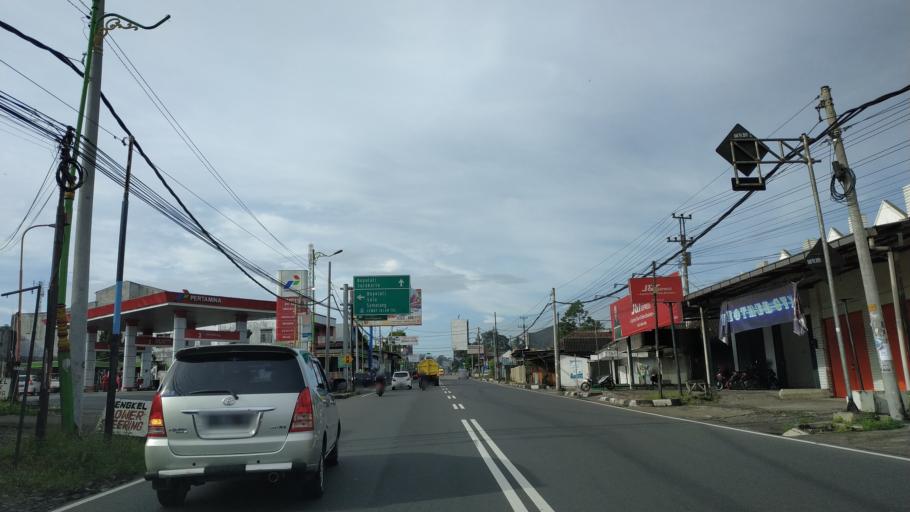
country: ID
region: Central Java
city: Salatiga
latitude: -7.3602
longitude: 110.5135
